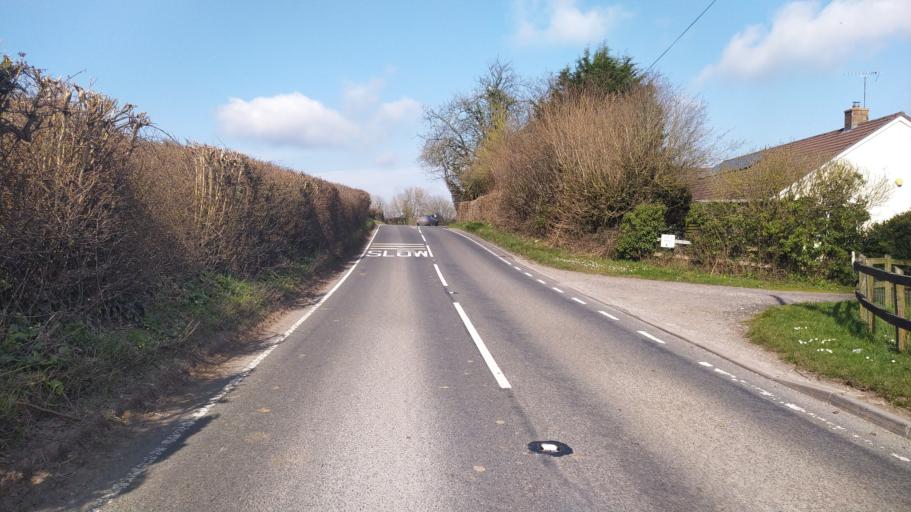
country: GB
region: England
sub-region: Somerset
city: Crewkerne
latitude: 50.8533
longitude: -2.7736
